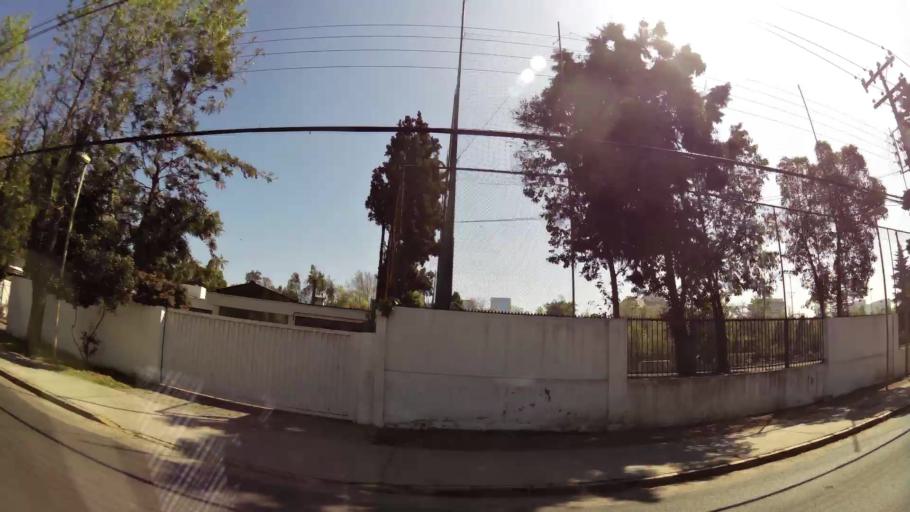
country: CL
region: Santiago Metropolitan
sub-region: Provincia de Santiago
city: Villa Presidente Frei, Nunoa, Santiago, Chile
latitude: -33.4164
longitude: -70.5778
